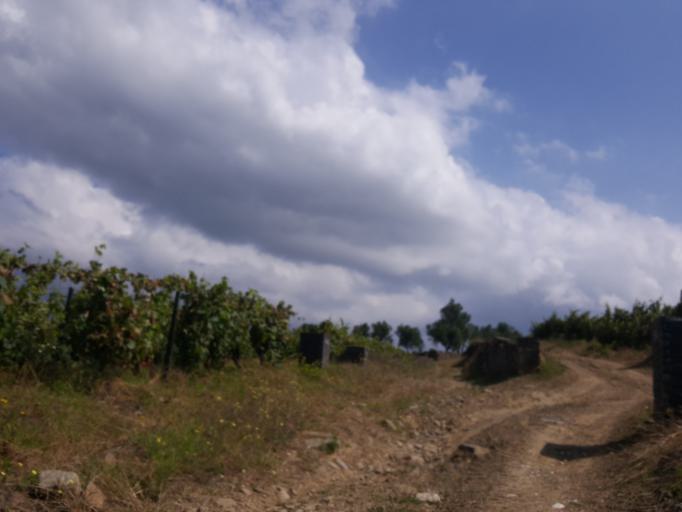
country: PT
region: Vila Real
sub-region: Mesao Frio
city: Mesao Frio
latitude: 41.1724
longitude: -7.8473
